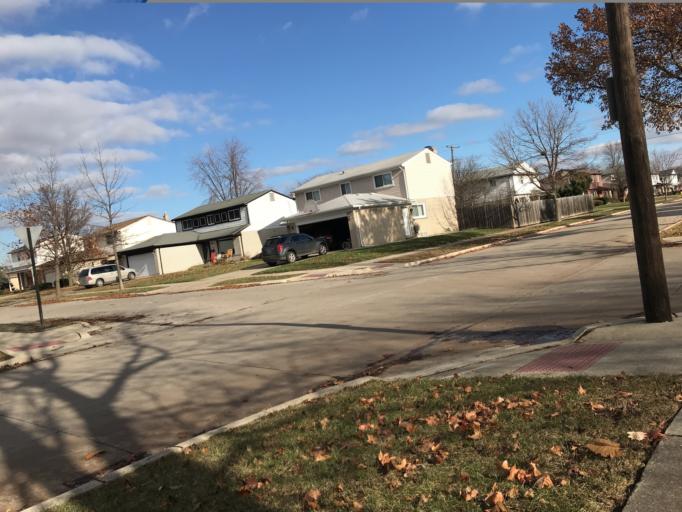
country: US
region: Michigan
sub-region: Oakland County
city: Berkley
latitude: 42.4851
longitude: -83.1981
